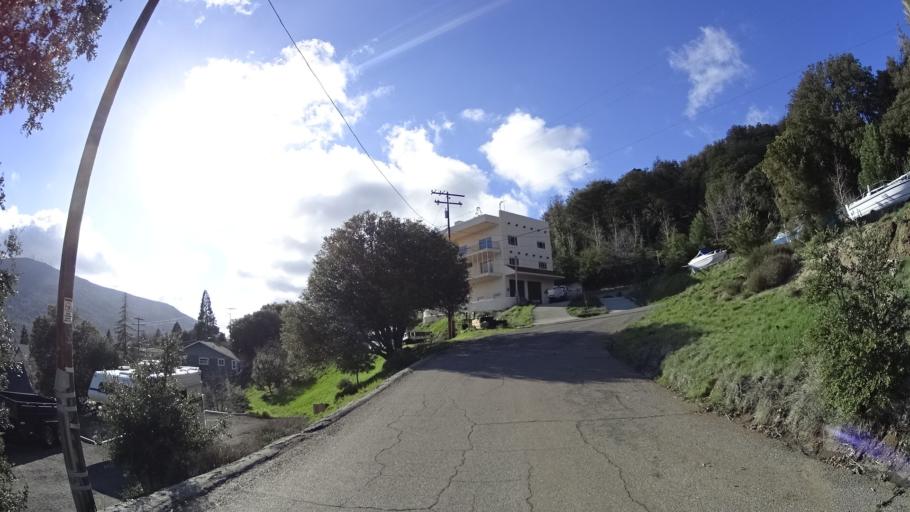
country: US
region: California
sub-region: San Diego County
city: Julian
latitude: 32.9938
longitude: -116.5811
